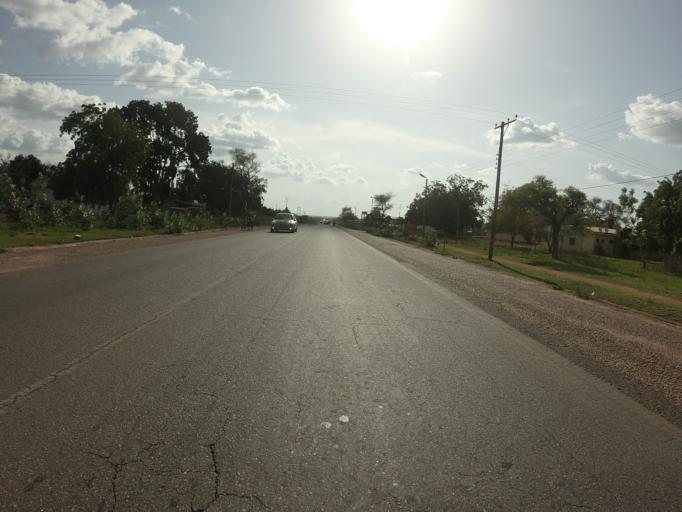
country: GH
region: Upper East
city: Bolgatanga
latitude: 10.8032
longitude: -0.8690
